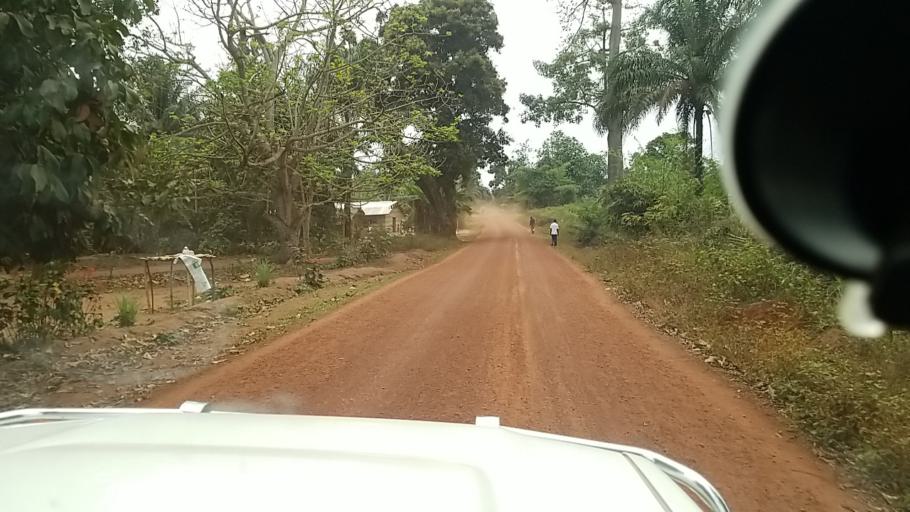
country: CD
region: Equateur
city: Libenge
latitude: 3.7243
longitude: 18.7709
